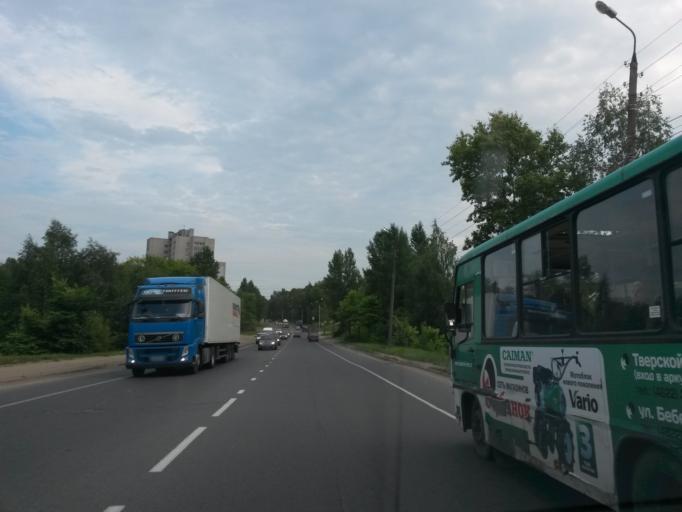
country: RU
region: Jaroslavl
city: Yaroslavl
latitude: 57.5871
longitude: 39.8204
